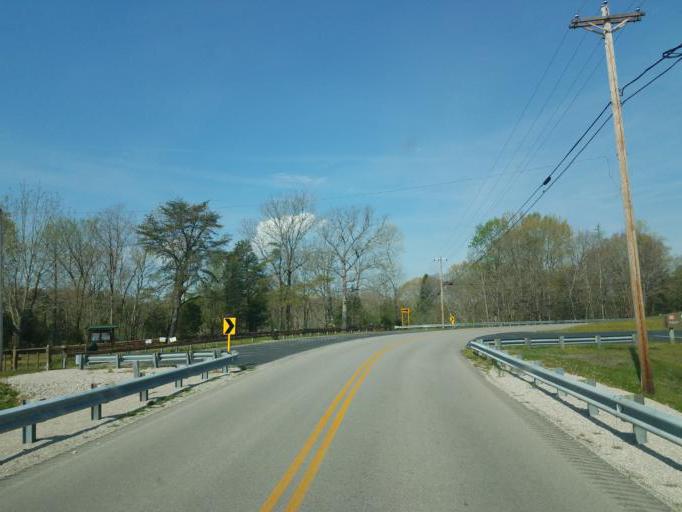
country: US
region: Kentucky
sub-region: Edmonson County
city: Brownsville
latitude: 37.2774
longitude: -86.2482
